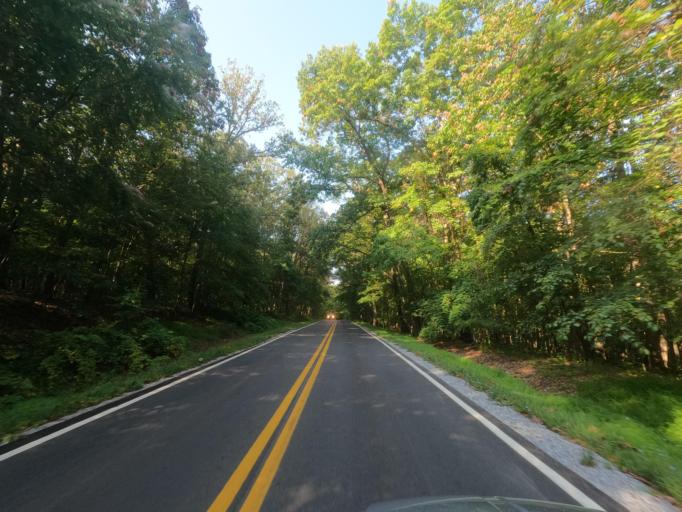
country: US
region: Maryland
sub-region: Carroll County
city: Eldersburg
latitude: 39.4264
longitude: -76.9300
